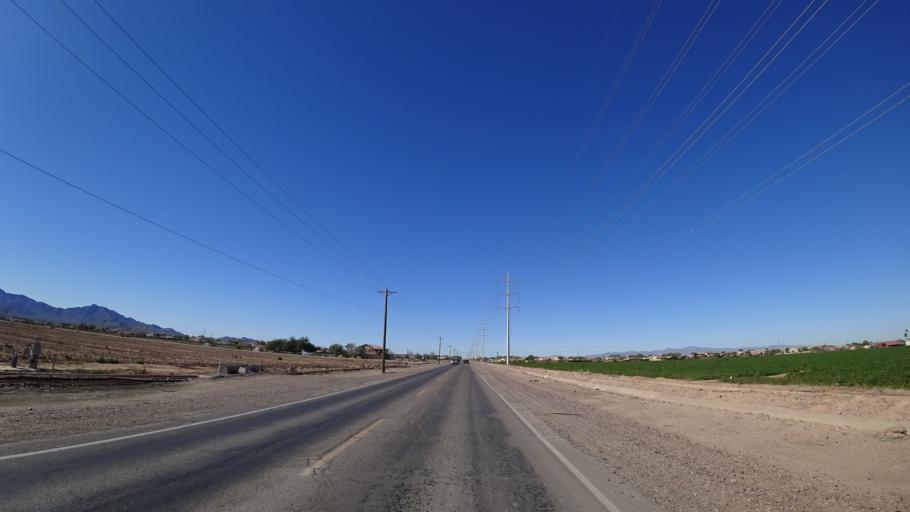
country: US
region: Arizona
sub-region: Maricopa County
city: Tolleson
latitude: 33.4065
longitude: -112.2684
